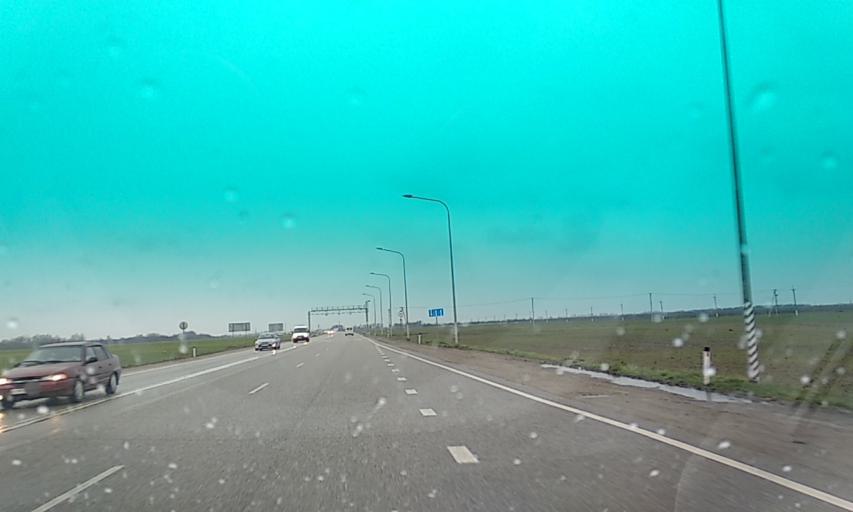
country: RU
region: Krasnodarskiy
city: Belorechensk
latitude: 44.8275
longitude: 39.8446
